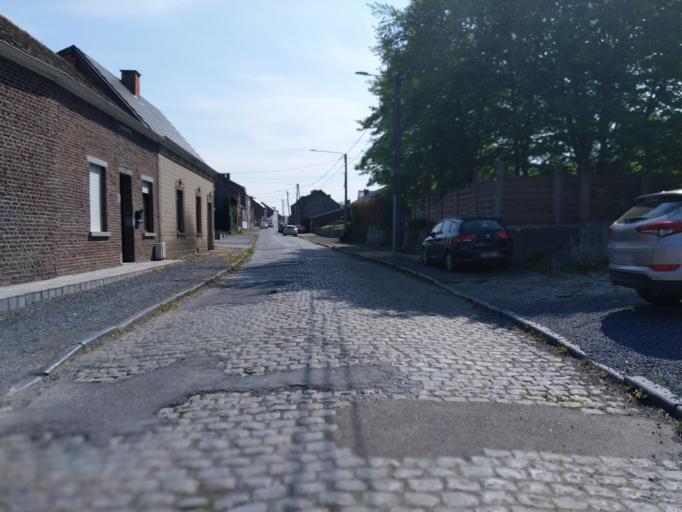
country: BE
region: Wallonia
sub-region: Province du Hainaut
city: Mons
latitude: 50.4621
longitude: 4.0337
